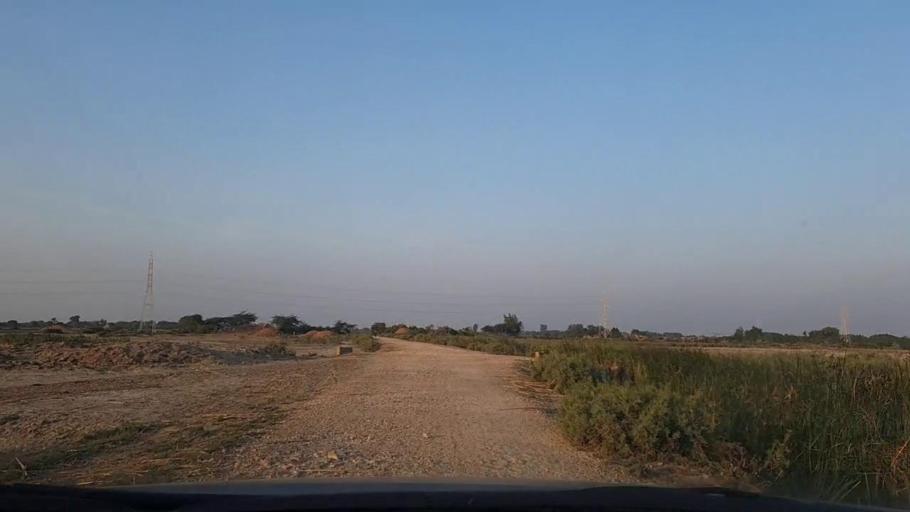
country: PK
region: Sindh
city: Mirpur Sakro
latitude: 24.5592
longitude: 67.6580
